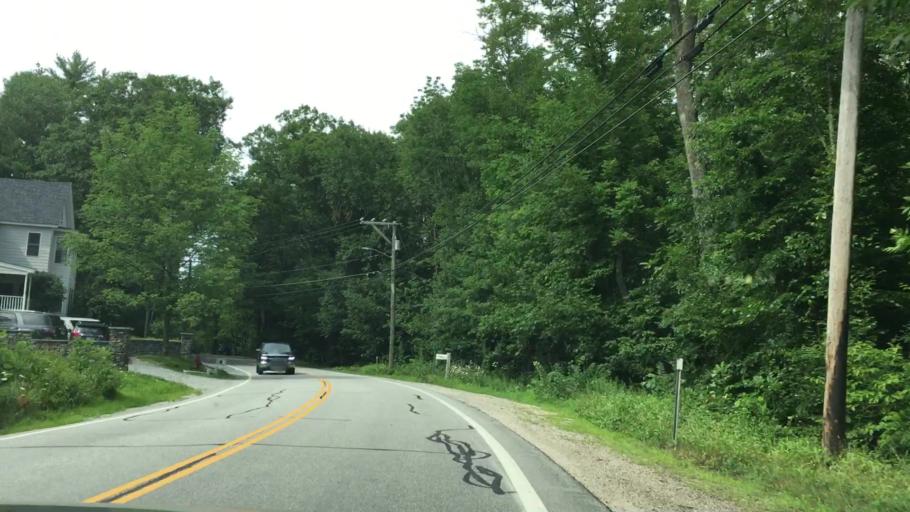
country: US
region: New Hampshire
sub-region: Hillsborough County
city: Antrim
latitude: 43.0362
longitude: -71.9355
